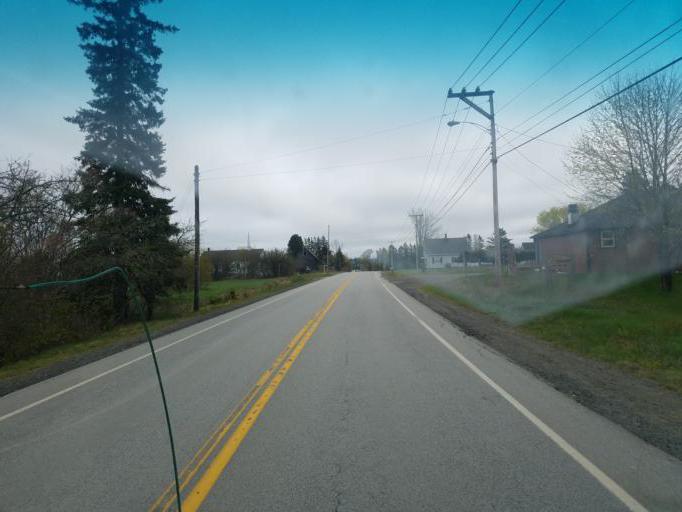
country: US
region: Maine
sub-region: Washington County
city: Eastport
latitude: 44.8166
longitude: -67.0648
